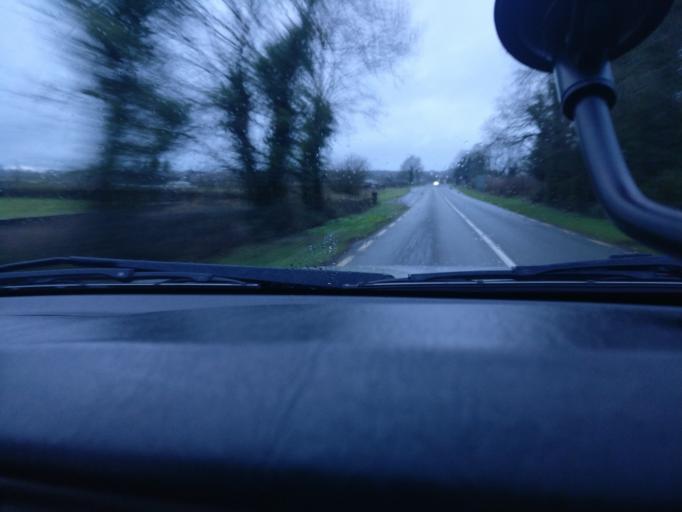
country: IE
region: Connaught
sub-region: County Galway
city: Ballinasloe
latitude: 53.2705
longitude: -8.3902
